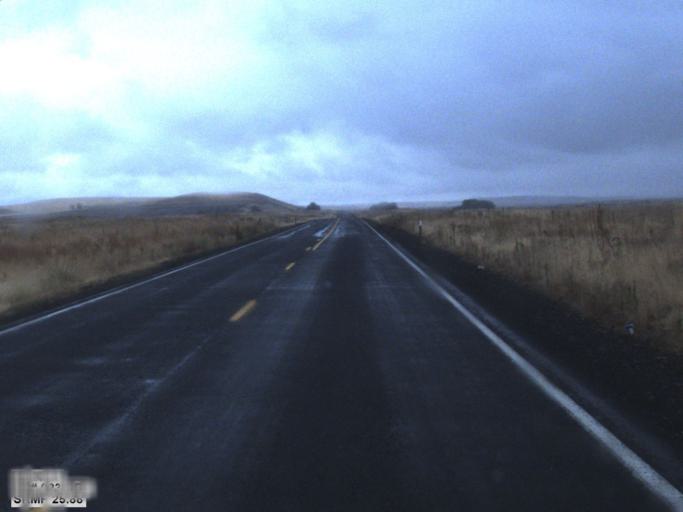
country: US
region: Washington
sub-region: Spokane County
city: Cheney
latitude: 47.1141
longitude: -117.8011
